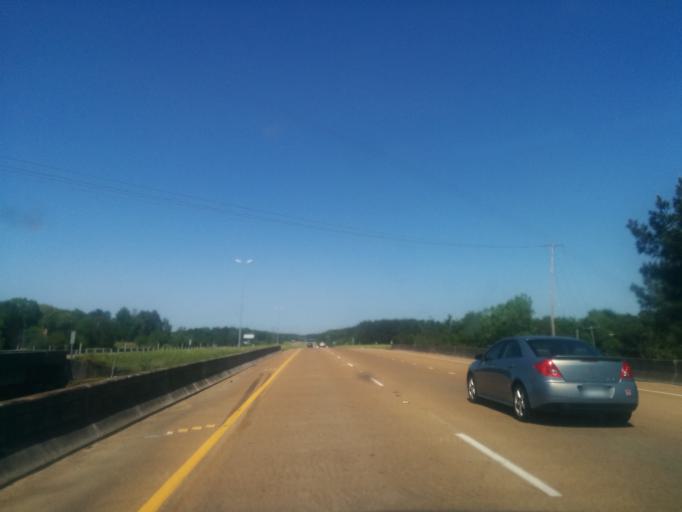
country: US
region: Mississippi
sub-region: Madison County
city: Ridgeland
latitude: 32.4001
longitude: -90.1769
